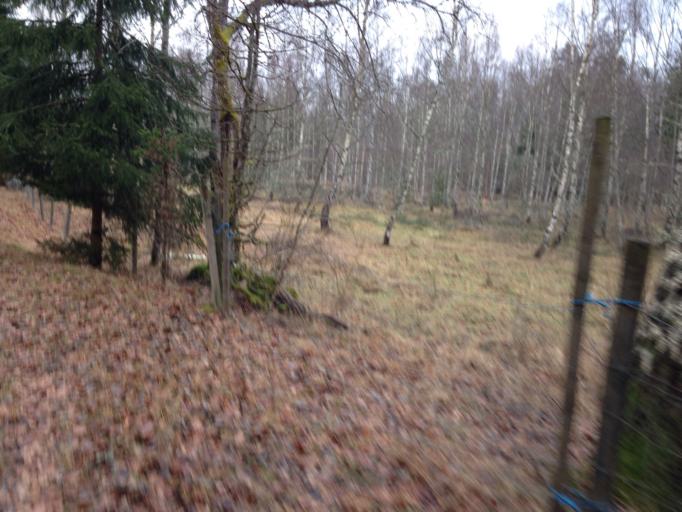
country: SE
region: Joenkoeping
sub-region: Varnamo Kommun
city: Bor
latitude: 57.0357
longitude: 14.1833
